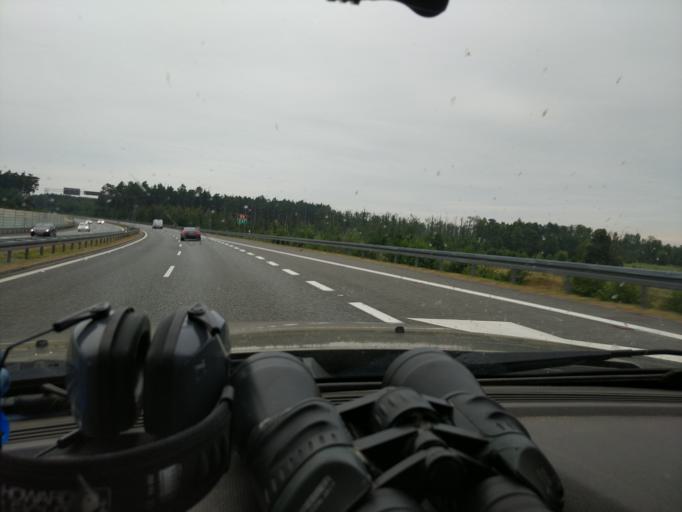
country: PL
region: Masovian Voivodeship
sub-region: Powiat wyszkowski
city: Wyszkow
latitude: 52.5600
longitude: 21.4665
